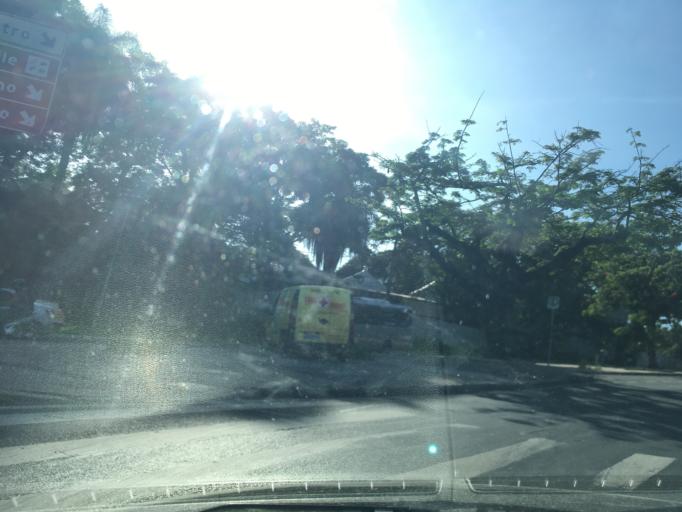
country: BR
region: Minas Gerais
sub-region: Belo Horizonte
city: Belo Horizonte
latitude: -19.8629
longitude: -43.9744
